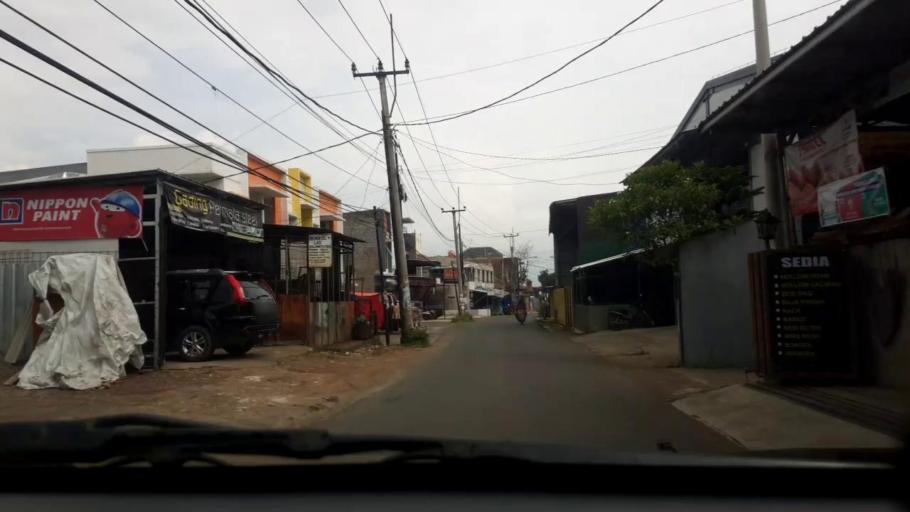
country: ID
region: West Java
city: Cileunyi
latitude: -6.9432
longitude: 107.7259
